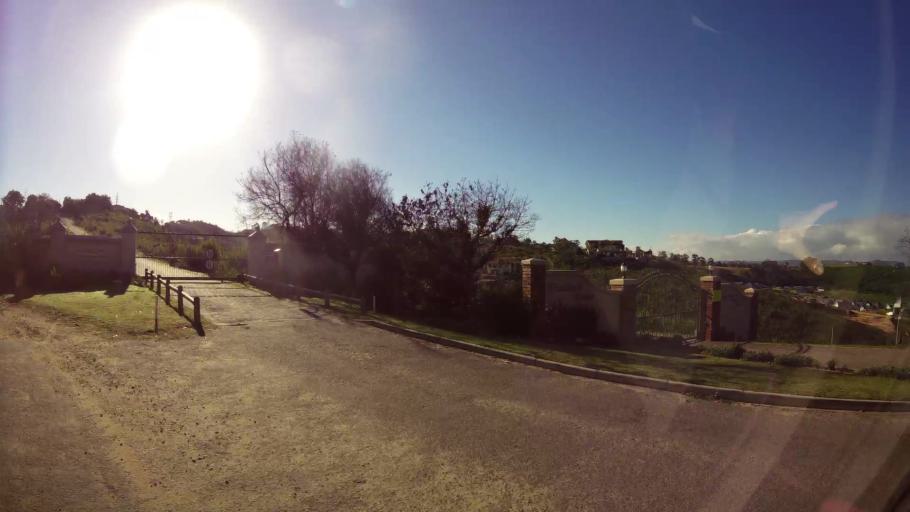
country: ZA
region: Western Cape
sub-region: Eden District Municipality
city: Knysna
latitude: -34.0225
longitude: 23.0093
